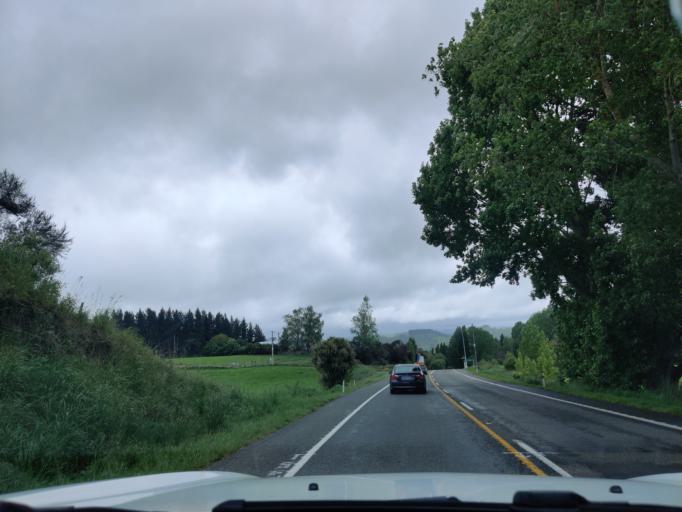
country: NZ
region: Manawatu-Wanganui
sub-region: Ruapehu District
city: Waiouru
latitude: -39.6476
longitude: 175.7681
